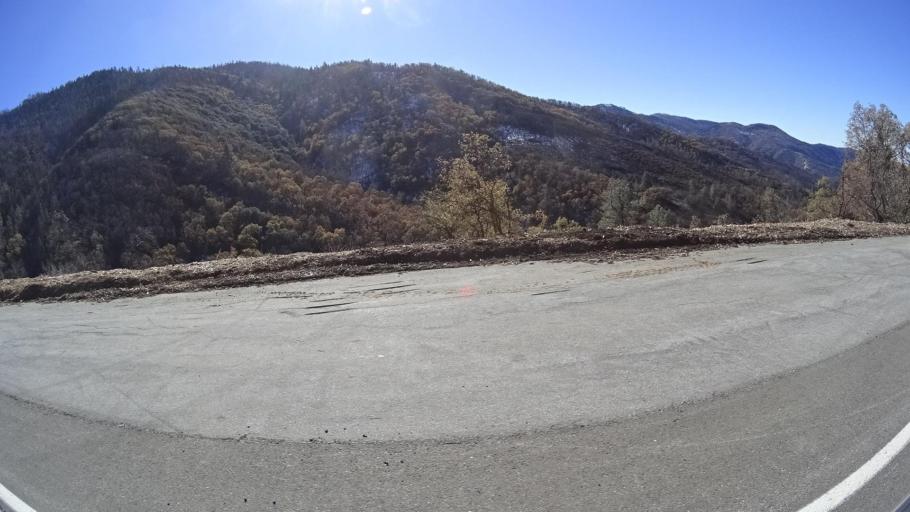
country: US
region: California
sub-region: Kern County
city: Alta Sierra
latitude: 35.7420
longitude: -118.5761
